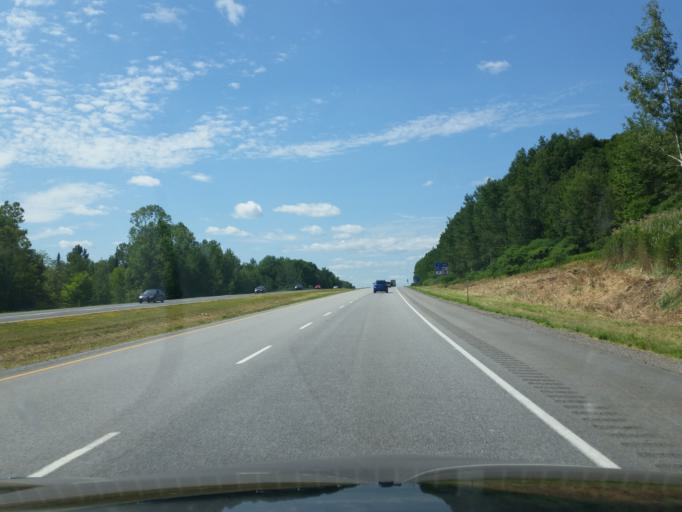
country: CA
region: Quebec
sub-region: Monteregie
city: Hudson
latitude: 45.4503
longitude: -74.2099
